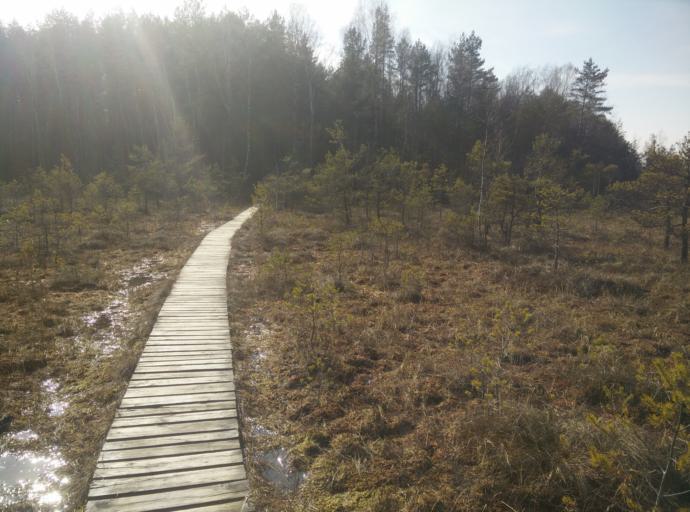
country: LT
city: Trakai
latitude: 54.6402
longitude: 24.9795
